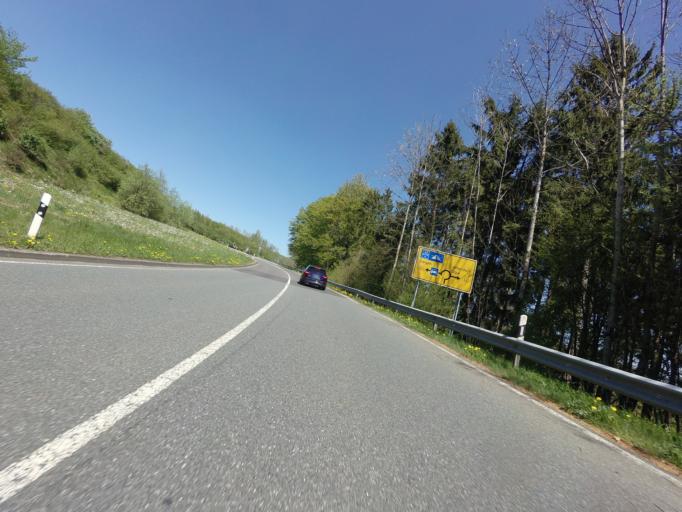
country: DE
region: North Rhine-Westphalia
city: Kreuztal
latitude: 51.0088
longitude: 7.9416
